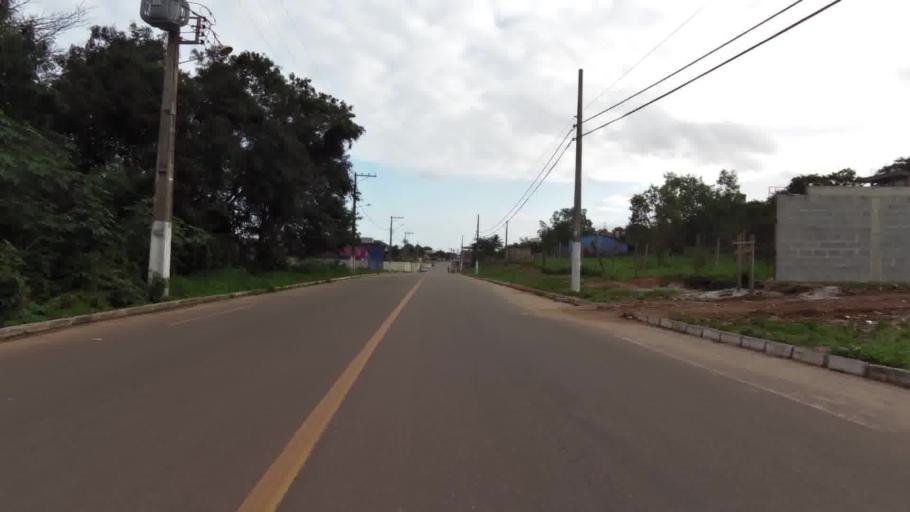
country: BR
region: Espirito Santo
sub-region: Piuma
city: Piuma
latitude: -20.7975
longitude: -40.6405
